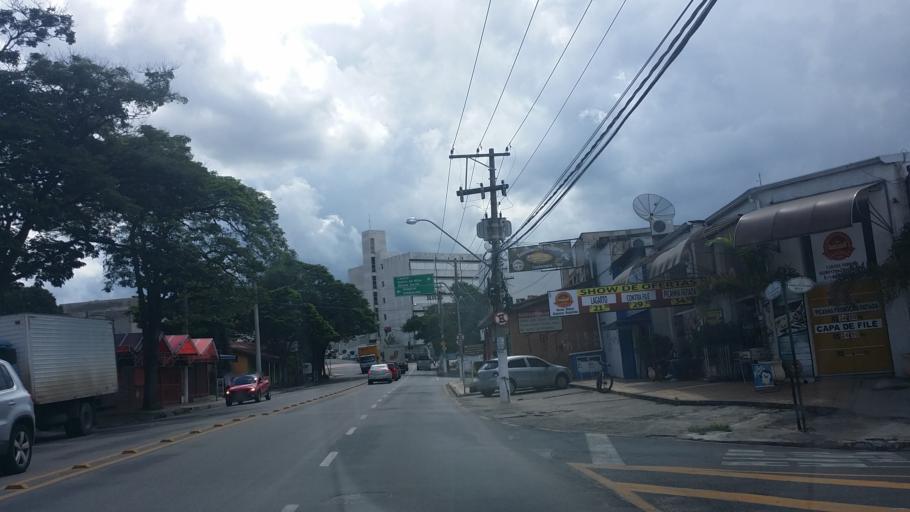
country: BR
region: Sao Paulo
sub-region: Itupeva
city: Itupeva
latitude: -23.1557
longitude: -47.0552
